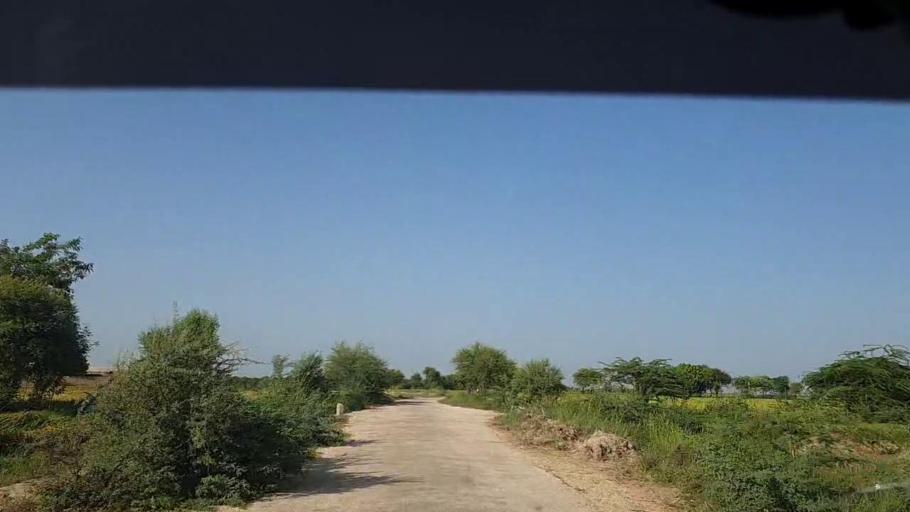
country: PK
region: Sindh
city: Badin
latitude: 24.6841
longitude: 68.8411
